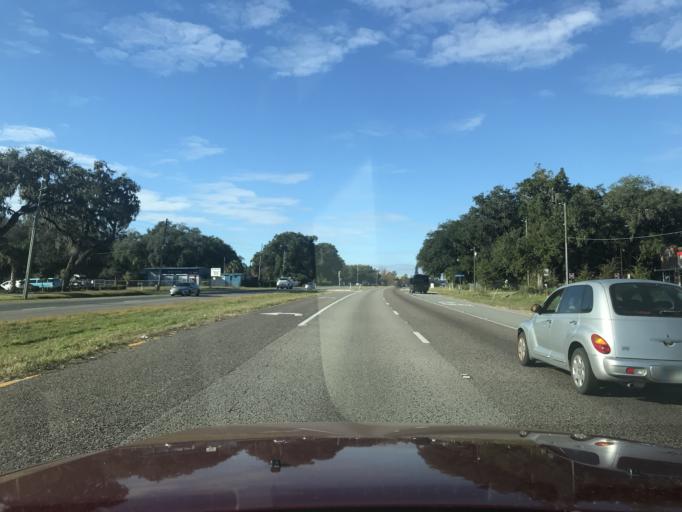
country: US
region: Florida
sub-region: Osceola County
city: Campbell
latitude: 28.2599
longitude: -81.4381
